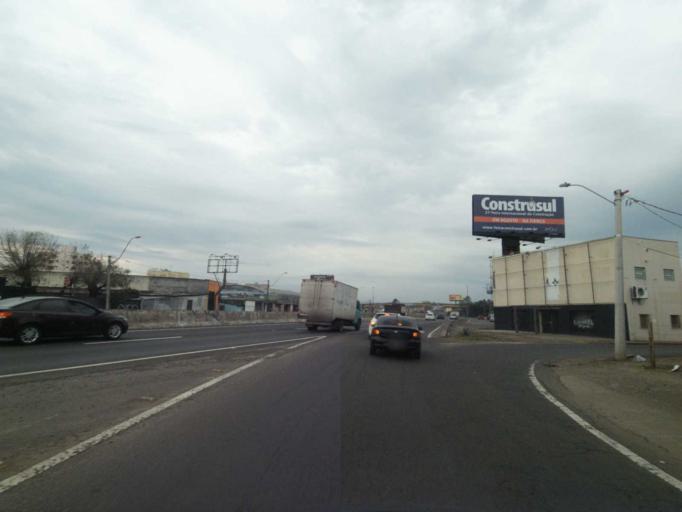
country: BR
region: Rio Grande do Sul
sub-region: Sao Leopoldo
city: Sao Leopoldo
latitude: -29.7629
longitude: -51.1532
